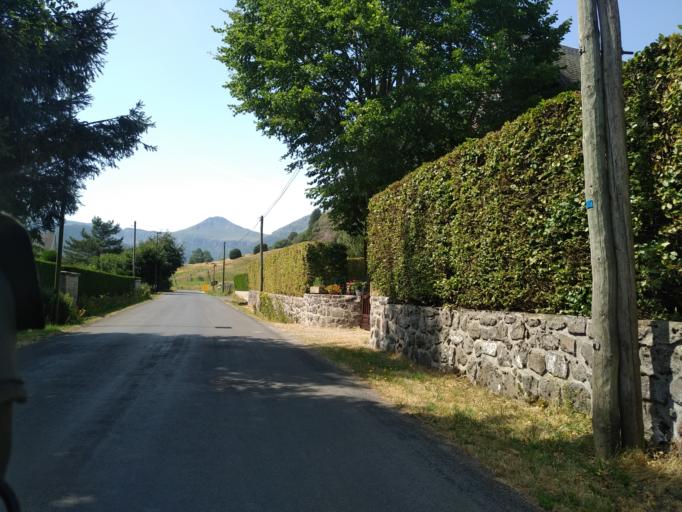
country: FR
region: Auvergne
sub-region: Departement du Cantal
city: Riom-es-Montagnes
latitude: 45.1569
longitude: 2.7031
